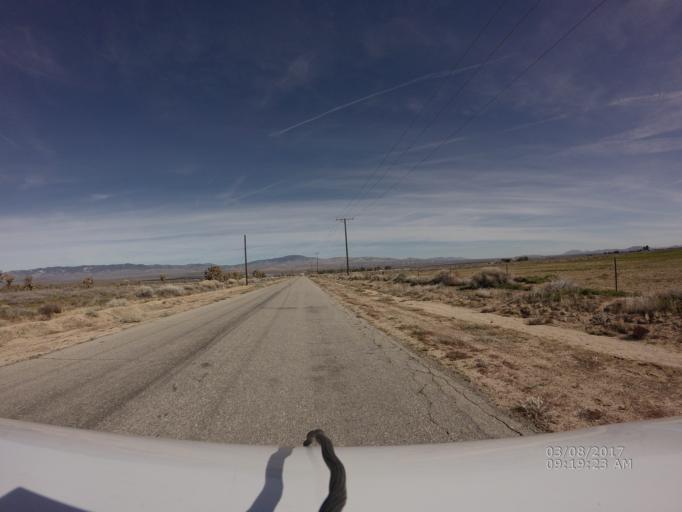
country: US
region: California
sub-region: Los Angeles County
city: Green Valley
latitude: 34.7921
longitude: -118.4666
